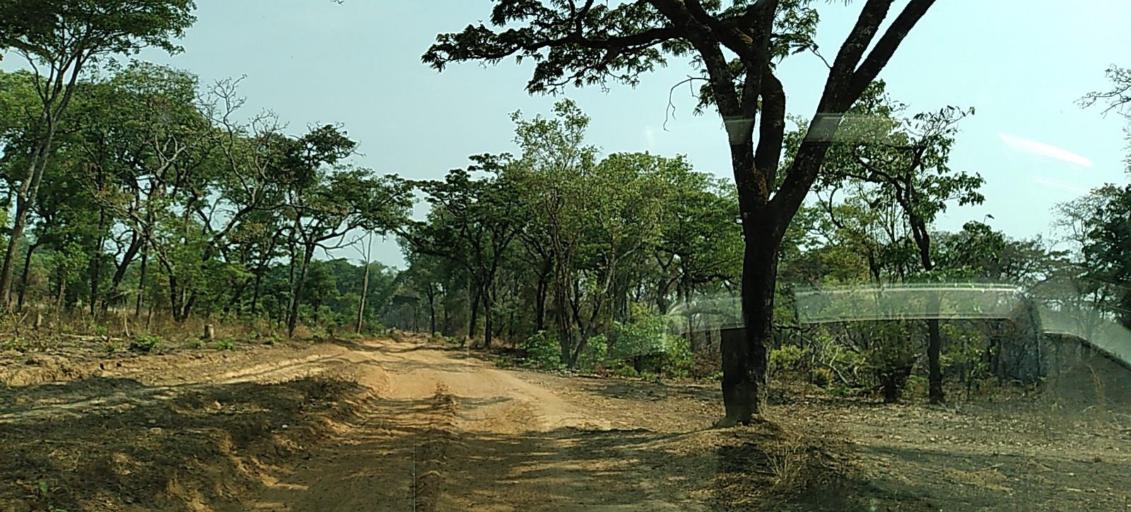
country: ZM
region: North-Western
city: Kansanshi
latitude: -12.0647
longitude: 26.8894
